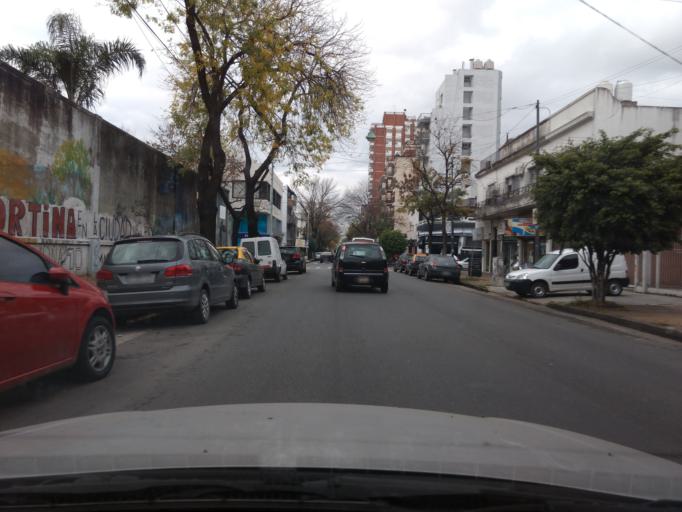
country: AR
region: Buenos Aires F.D.
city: Villa Santa Rita
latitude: -34.6210
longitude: -58.4987
